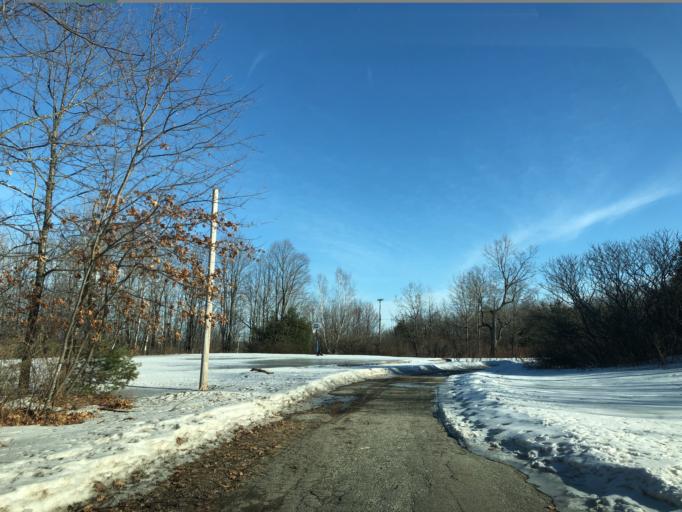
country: US
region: Maine
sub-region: Androscoggin County
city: Poland
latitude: 44.0271
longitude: -70.3605
